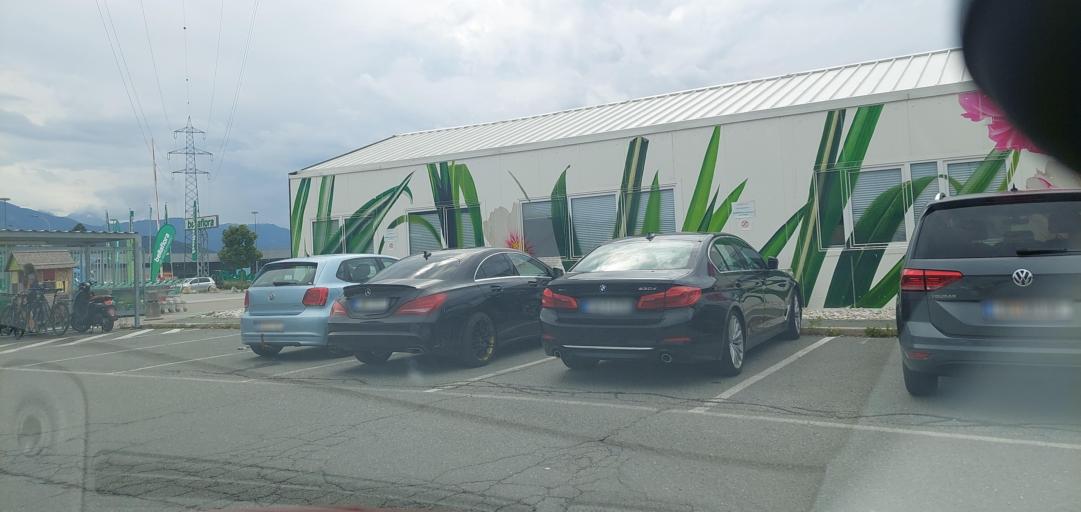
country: AT
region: Carinthia
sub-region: Villach Stadt
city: Villach
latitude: 46.6058
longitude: 13.8655
